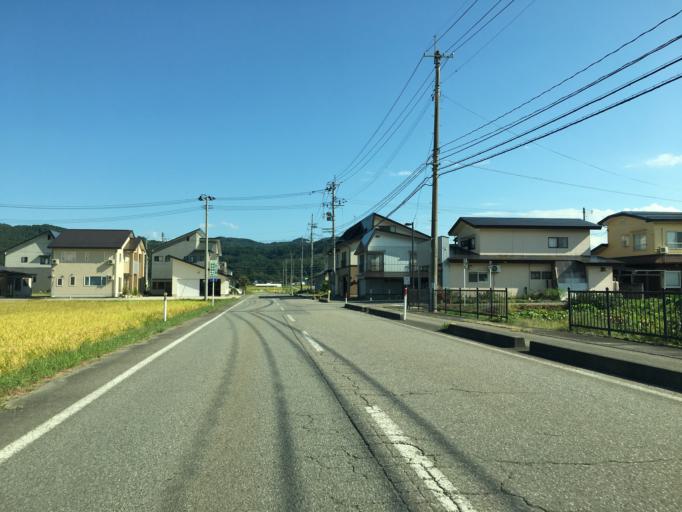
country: JP
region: Fukushima
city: Kitakata
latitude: 37.5912
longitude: 139.6570
